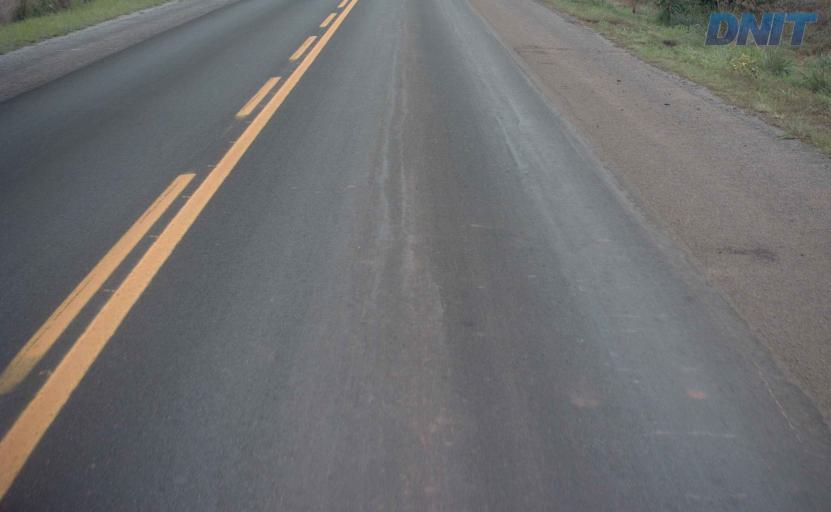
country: BR
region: Goias
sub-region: Padre Bernardo
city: Padre Bernardo
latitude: -15.2156
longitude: -48.5050
